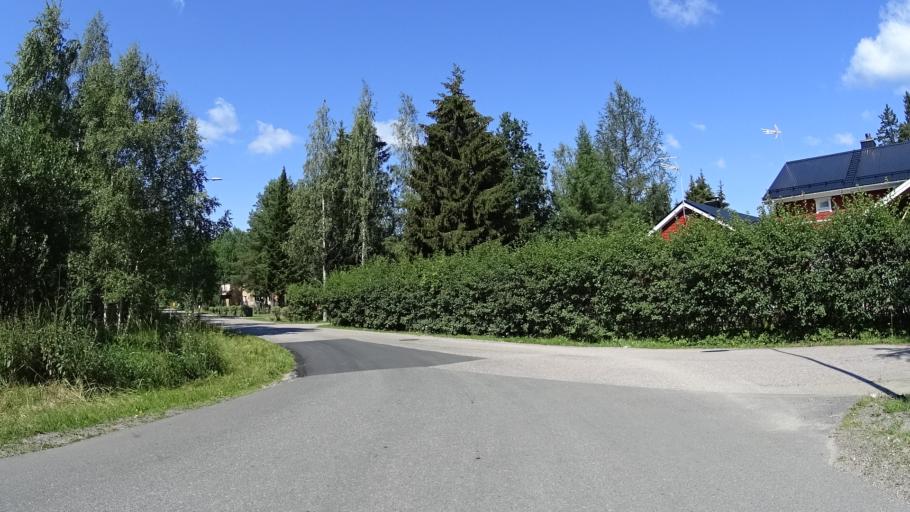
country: FI
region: Uusimaa
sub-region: Helsinki
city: Jaervenpaeae
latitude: 60.4474
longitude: 25.1069
